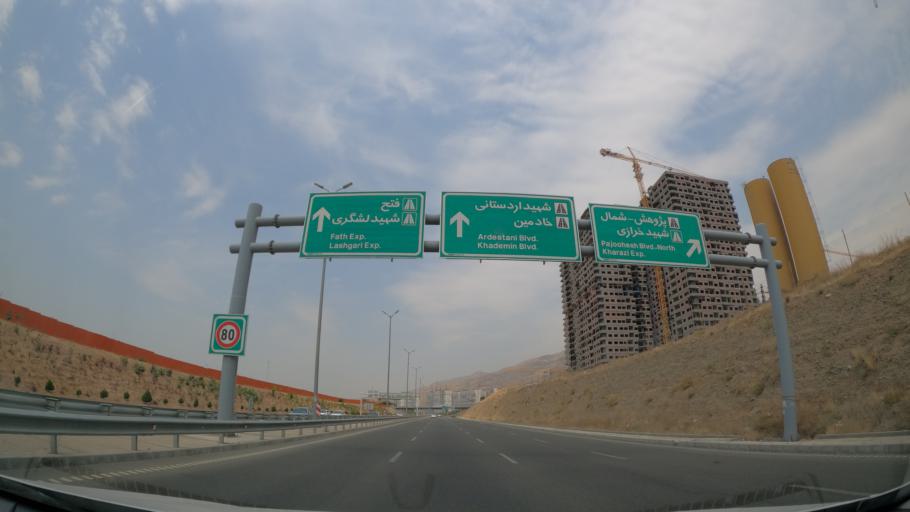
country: IR
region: Tehran
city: Shahr-e Qods
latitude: 35.7481
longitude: 51.1782
